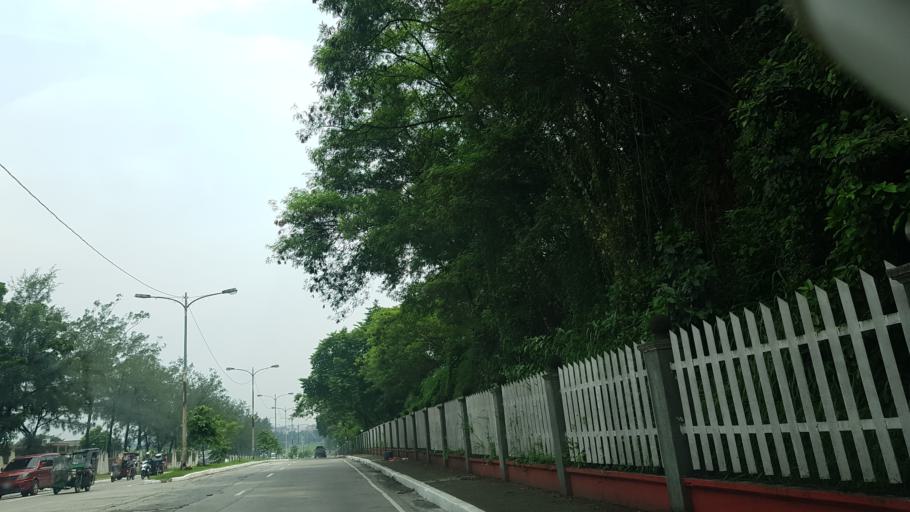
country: PH
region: Metro Manila
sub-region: Makati City
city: Makati City
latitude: 14.5239
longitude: 121.0464
